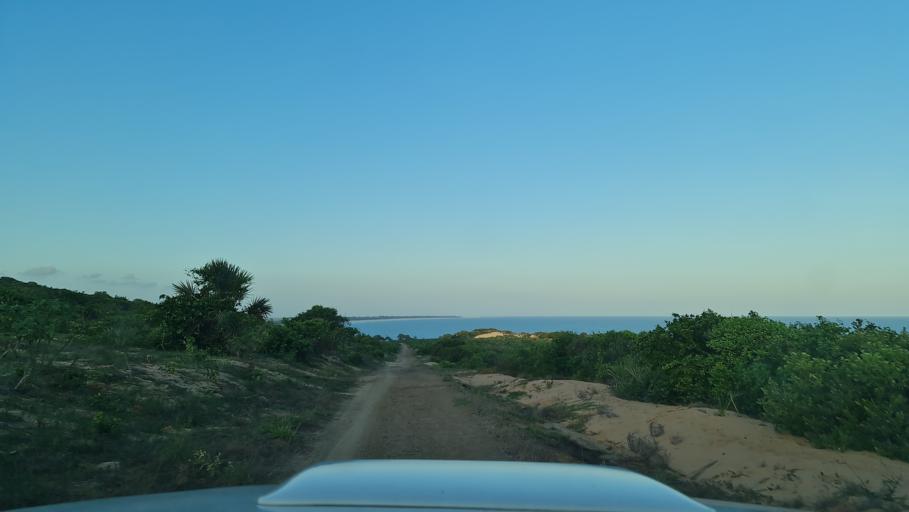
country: MZ
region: Nampula
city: Ilha de Mocambique
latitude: -15.6324
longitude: 40.4185
